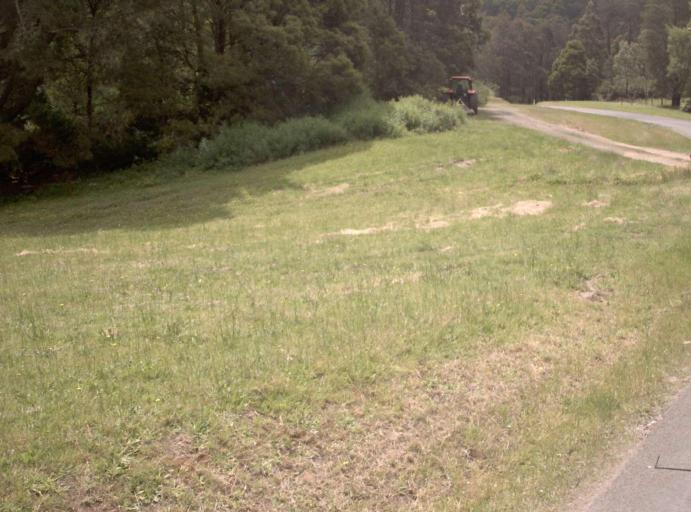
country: AU
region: Victoria
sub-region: Latrobe
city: Traralgon
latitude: -38.4285
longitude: 146.5659
